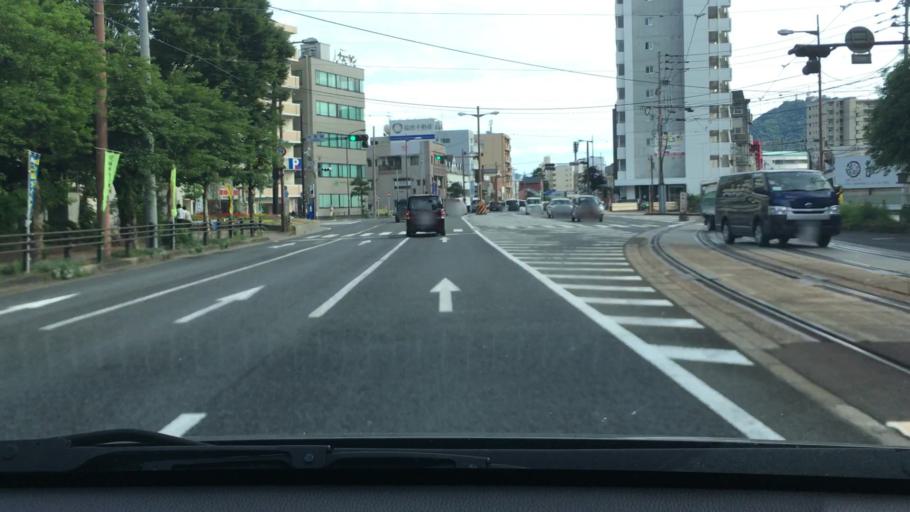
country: JP
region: Nagasaki
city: Nagasaki-shi
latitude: 32.7818
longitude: 129.8624
